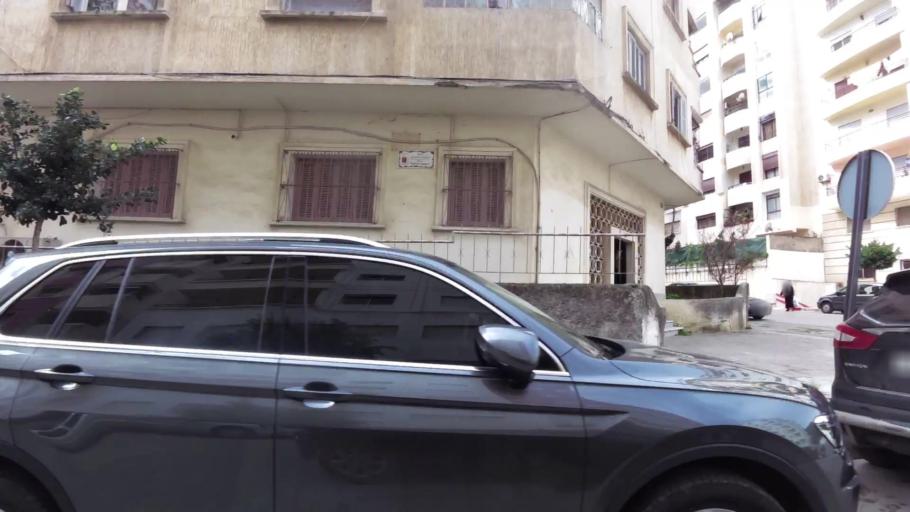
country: MA
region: Tanger-Tetouan
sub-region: Tanger-Assilah
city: Tangier
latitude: 35.7777
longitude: -5.8206
